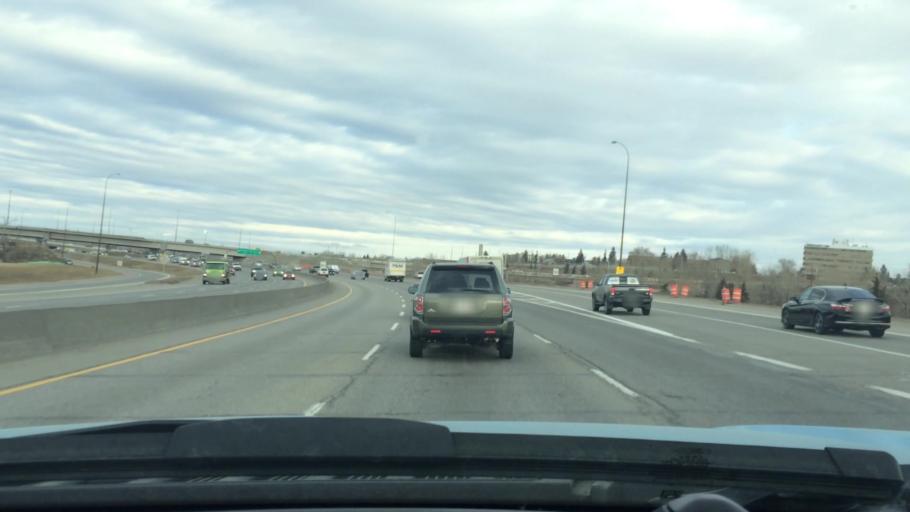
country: CA
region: Alberta
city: Calgary
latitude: 51.0327
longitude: -113.9979
